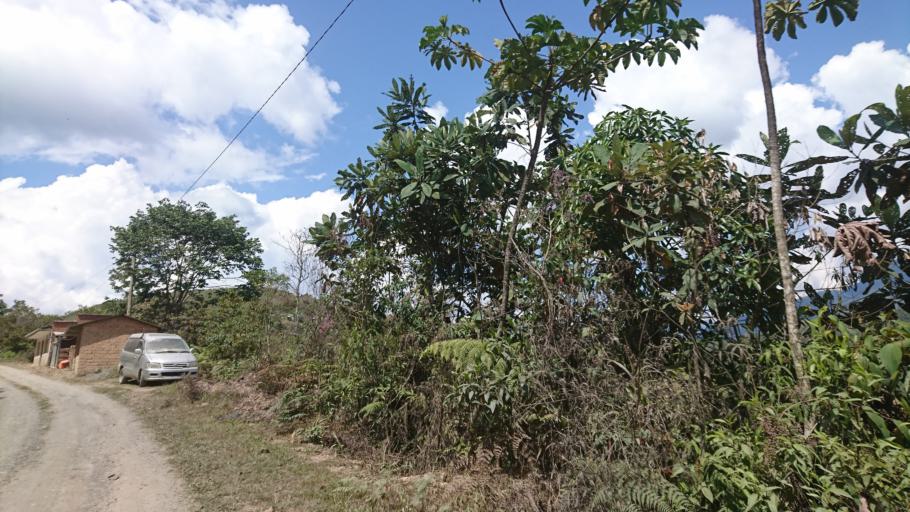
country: BO
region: La Paz
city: Coroico
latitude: -16.0774
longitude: -67.7818
